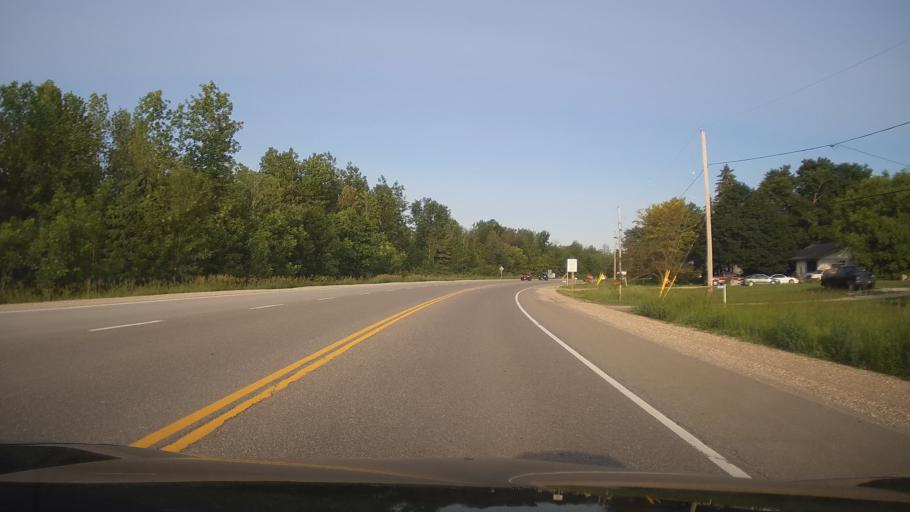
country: CA
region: Ontario
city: Perth
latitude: 44.8810
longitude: -76.3249
